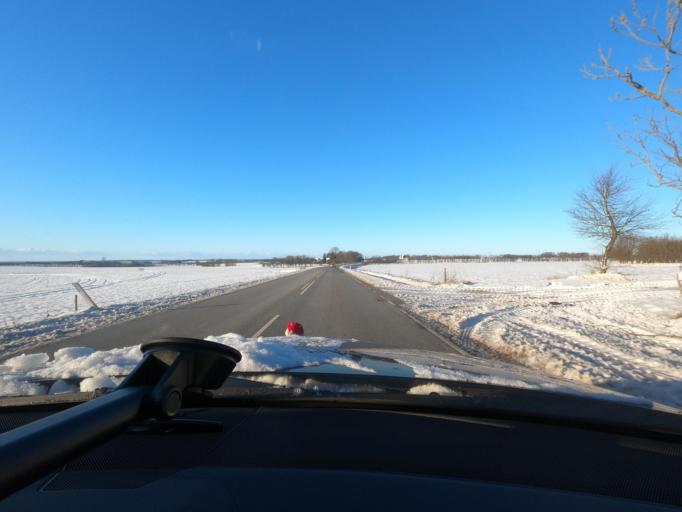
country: DK
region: South Denmark
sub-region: Aabenraa Kommune
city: Rodekro
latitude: 55.0917
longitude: 9.2013
